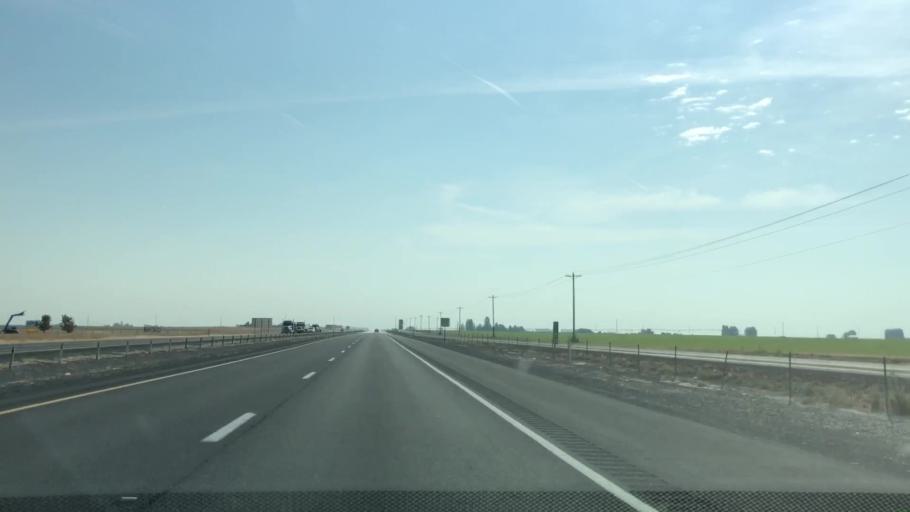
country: US
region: Washington
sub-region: Grant County
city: Moses Lake
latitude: 47.0968
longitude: -119.2338
